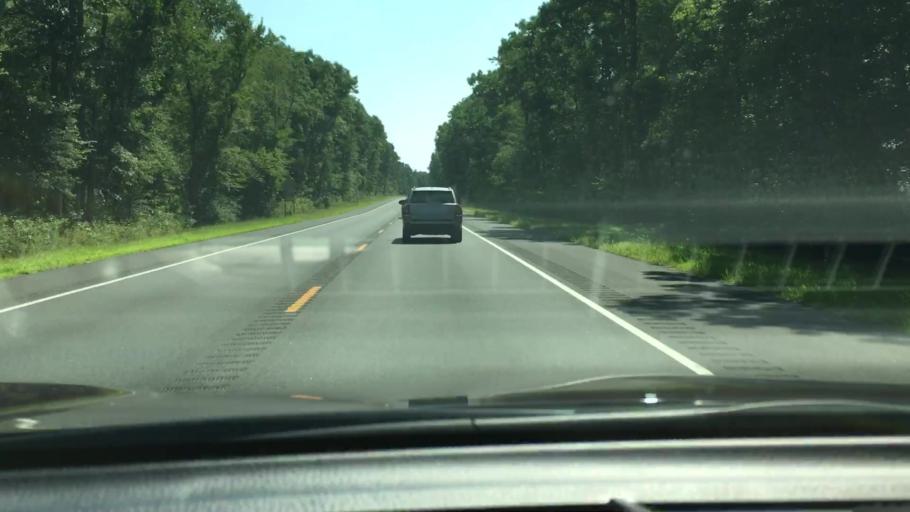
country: US
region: New Jersey
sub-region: Cape May County
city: Woodbine
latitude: 39.3172
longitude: -74.8411
